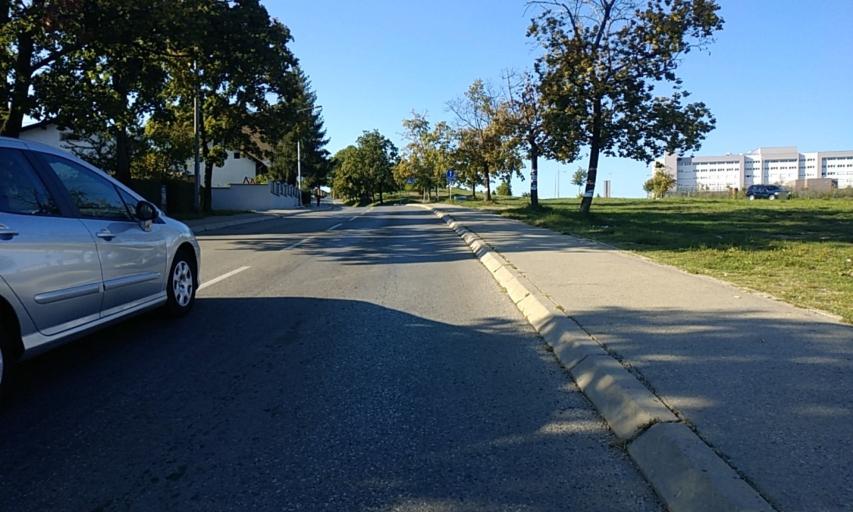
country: BA
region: Republika Srpska
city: Banja Luka
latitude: 44.7812
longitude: 17.1774
